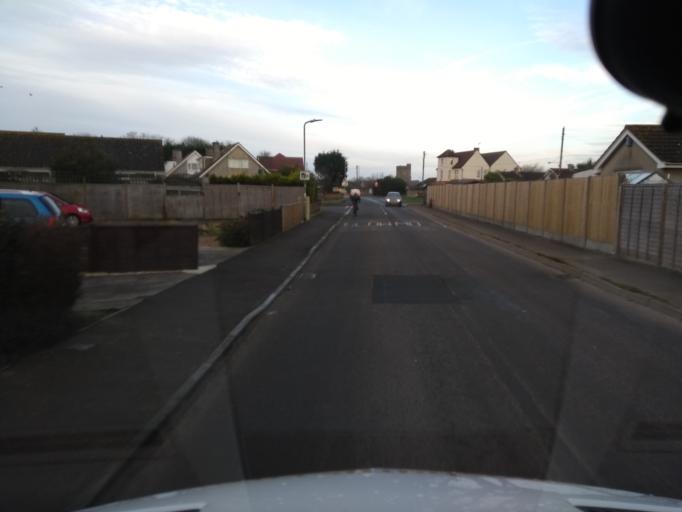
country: GB
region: England
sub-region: Somerset
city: Burnham-on-Sea
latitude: 51.2656
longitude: -3.0098
